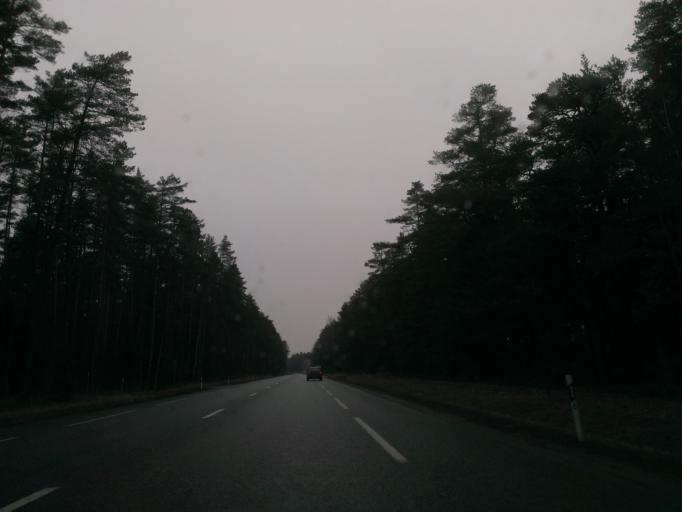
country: LV
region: Saulkrastu
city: Saulkrasti
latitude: 57.3617
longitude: 24.4375
